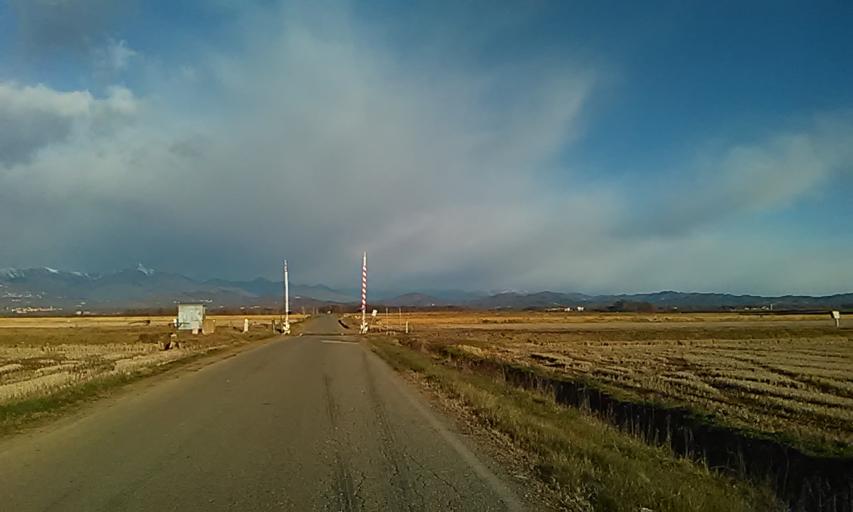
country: IT
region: Piedmont
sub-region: Provincia di Vercelli
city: Rovasenda
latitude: 45.5296
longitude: 8.2756
